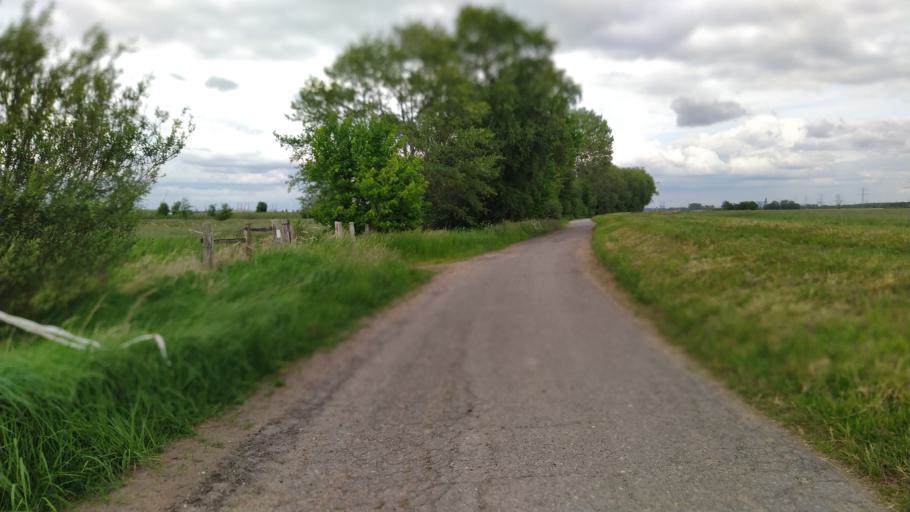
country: DE
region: Lower Saxony
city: Neu Wulmstorf
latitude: 53.4957
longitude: 9.8239
